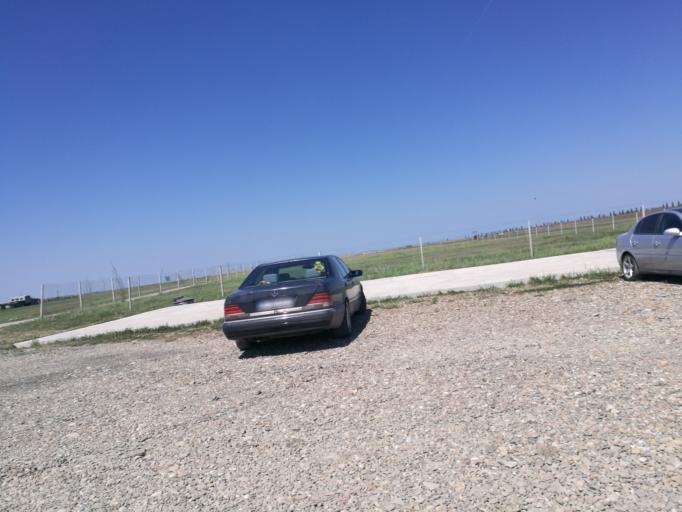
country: RO
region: Prahova
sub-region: Comuna Salciile
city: Salciile
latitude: 44.7795
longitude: 26.4713
